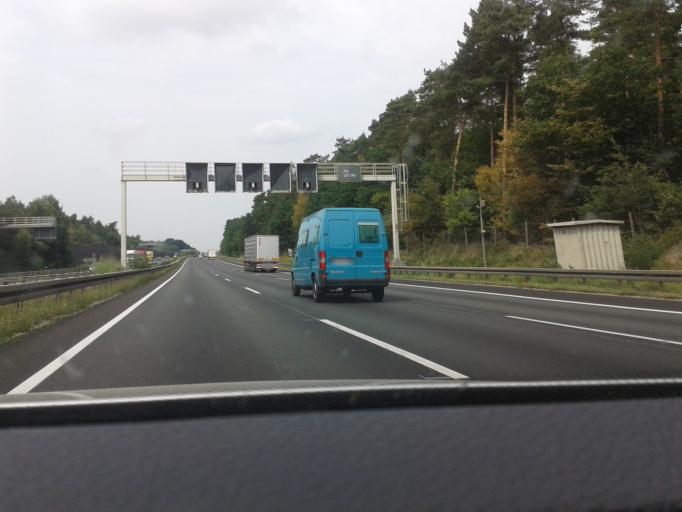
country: DE
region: Saxony-Anhalt
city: Harbke
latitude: 52.2228
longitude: 11.0486
